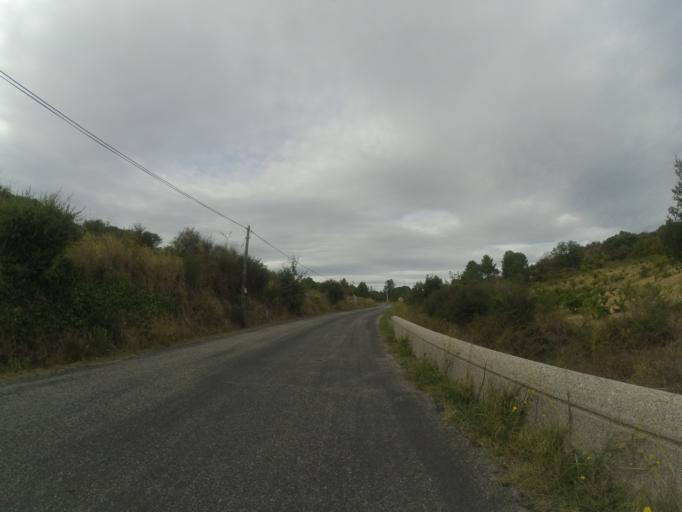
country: FR
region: Languedoc-Roussillon
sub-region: Departement des Pyrenees-Orientales
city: Pezilla-la-Riviere
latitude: 42.7043
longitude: 2.7631
